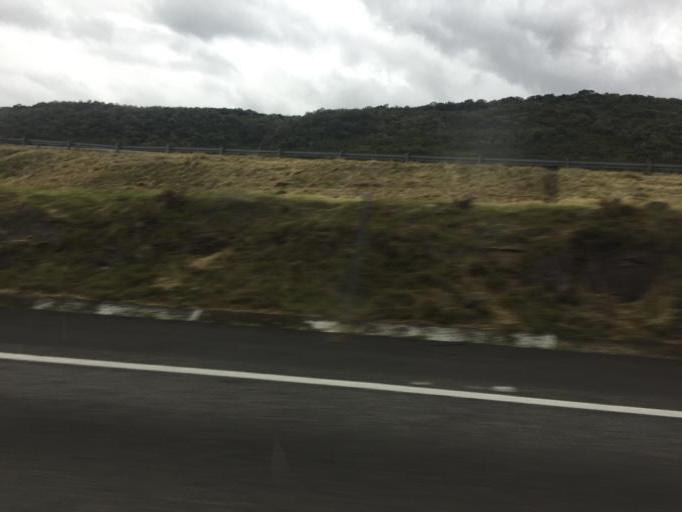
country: MX
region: Jalisco
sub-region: Zapotlan del Rey
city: Zapotlan del Rey
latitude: 20.5264
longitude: -103.0022
